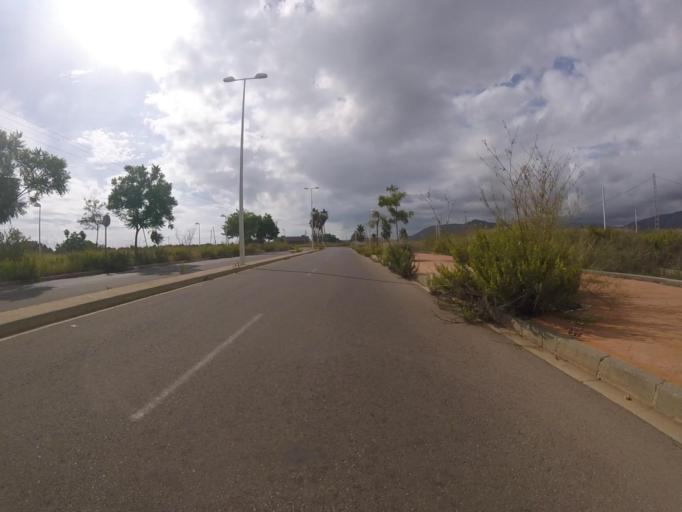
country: ES
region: Valencia
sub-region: Provincia de Castello
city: Orpesa/Oropesa del Mar
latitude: 40.1337
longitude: 0.1567
